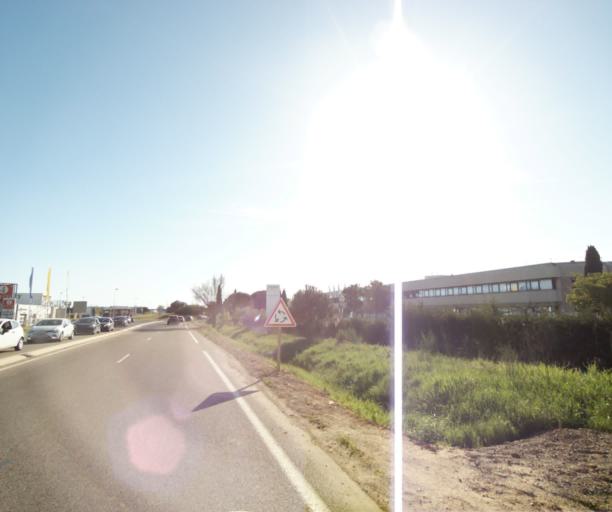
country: FR
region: Languedoc-Roussillon
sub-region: Departement de l'Herault
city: Perols
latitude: 43.5912
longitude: 3.9361
